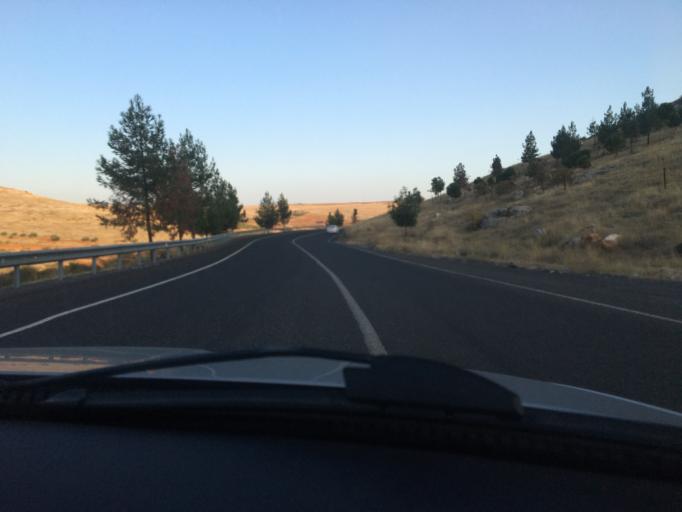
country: TR
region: Sanliurfa
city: Halfeti
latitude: 37.2267
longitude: 37.9564
